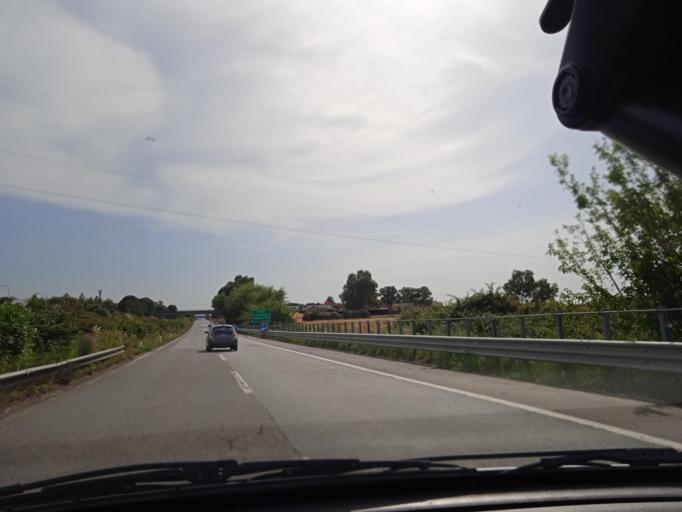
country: IT
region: Sicily
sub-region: Messina
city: San Filippo del Mela
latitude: 38.1897
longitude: 15.2685
